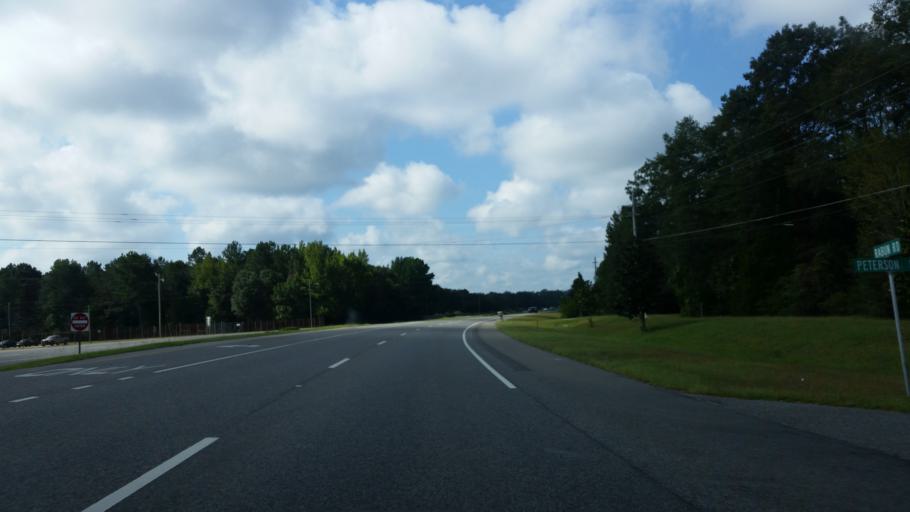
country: US
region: Alabama
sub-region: Baldwin County
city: Bay Minette
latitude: 30.9177
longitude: -87.7766
